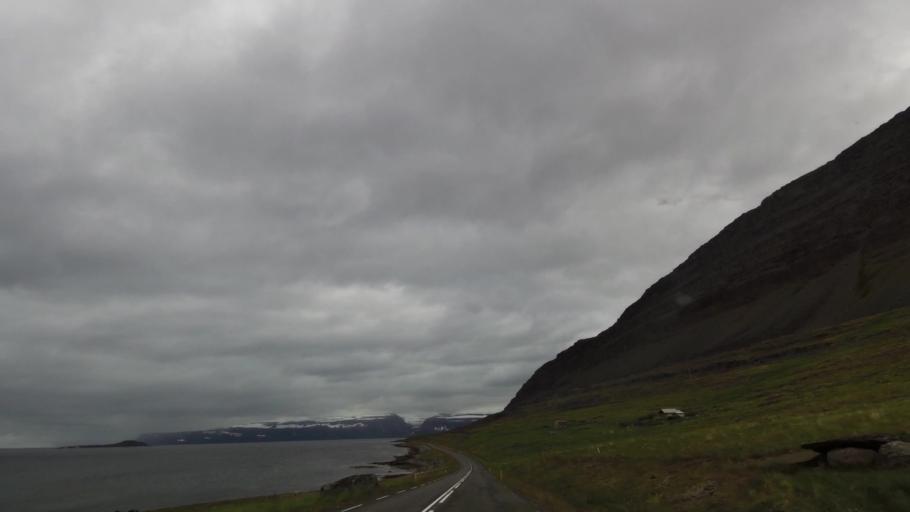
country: IS
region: Westfjords
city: Isafjoerdur
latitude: 66.0078
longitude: -22.7835
